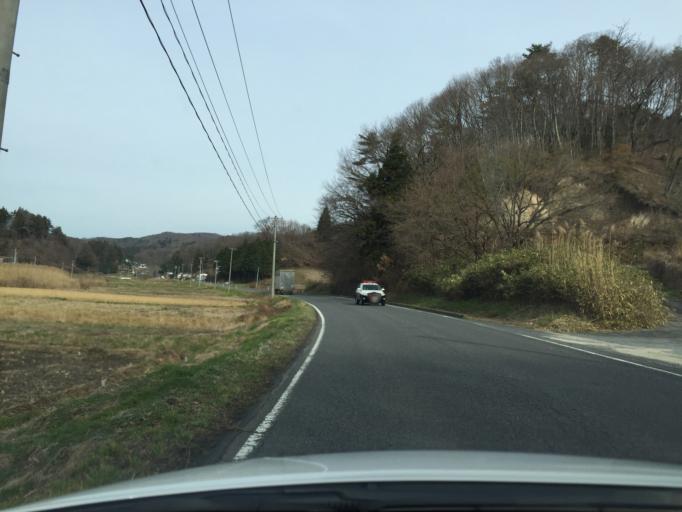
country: JP
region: Fukushima
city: Funehikimachi-funehiki
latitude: 37.3193
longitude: 140.6129
